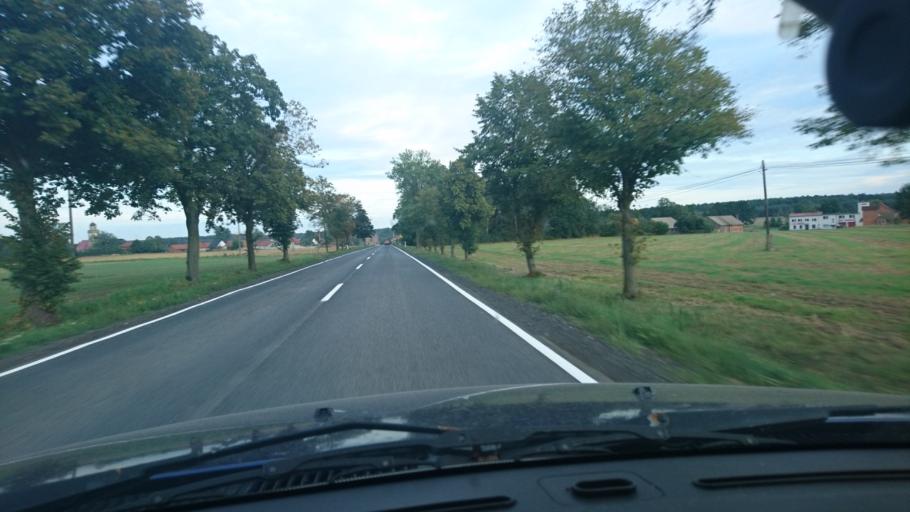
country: PL
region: Silesian Voivodeship
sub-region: Powiat lubliniecki
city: Sierakow Slaski
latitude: 50.8288
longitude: 18.5249
